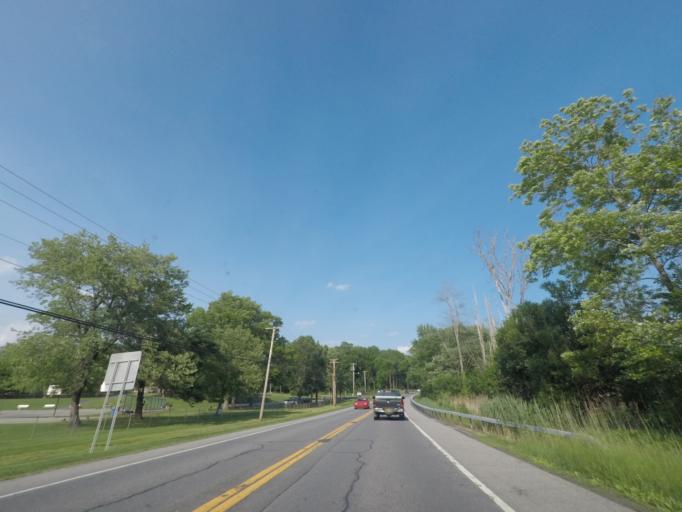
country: US
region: New York
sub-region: Orange County
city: Beaverdam Lake-Salisbury Mills
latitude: 41.4833
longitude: -74.1088
